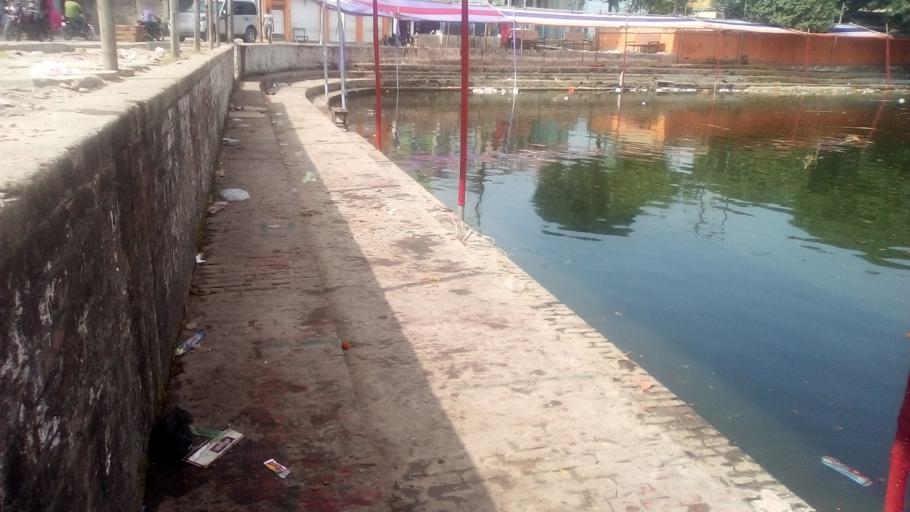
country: NP
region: Central Region
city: Janakpur
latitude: 26.7316
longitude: 85.9251
